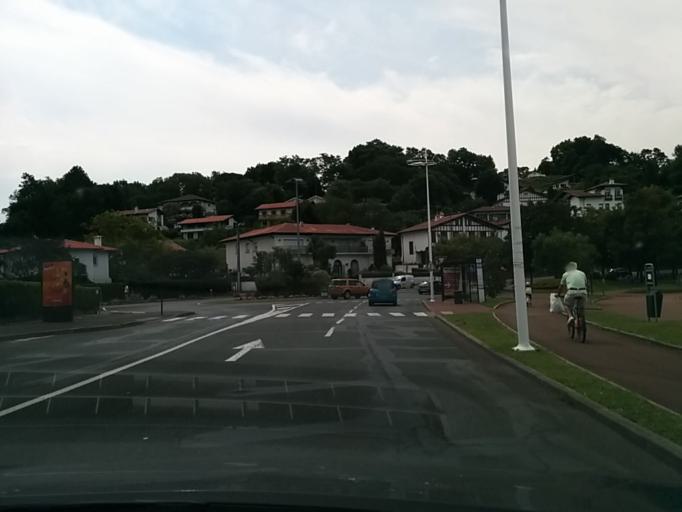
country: FR
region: Aquitaine
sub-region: Departement des Pyrenees-Atlantiques
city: Hendaye
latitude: 43.3657
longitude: -1.7700
